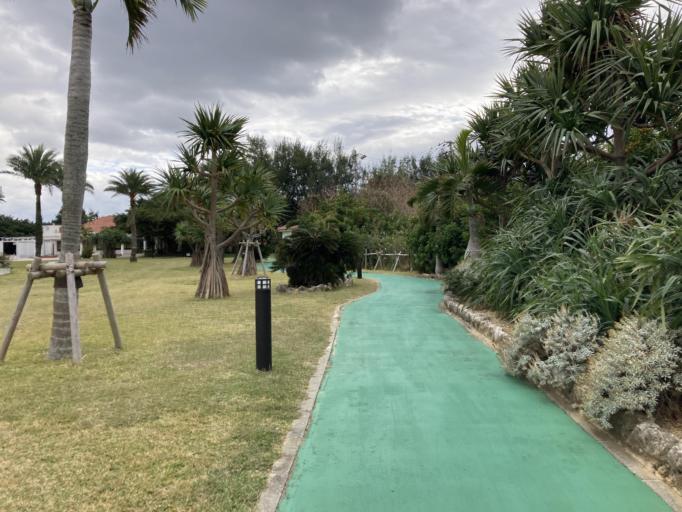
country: JP
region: Okinawa
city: Ishikawa
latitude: 26.4350
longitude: 127.7172
